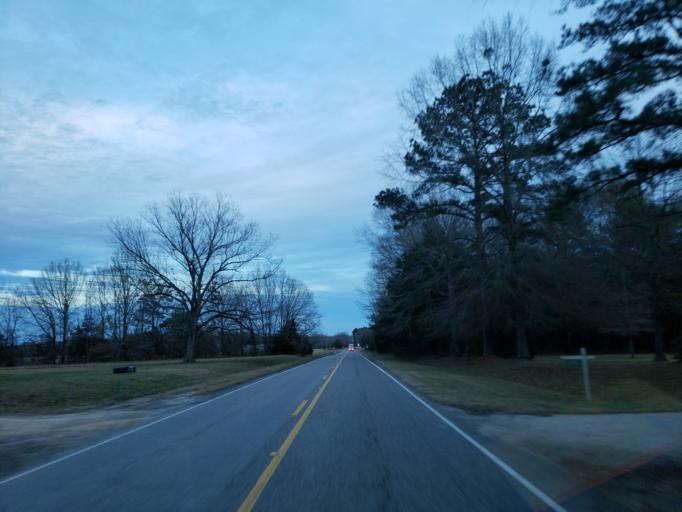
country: US
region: Alabama
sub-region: Sumter County
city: Livingston
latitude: 32.8316
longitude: -88.3142
